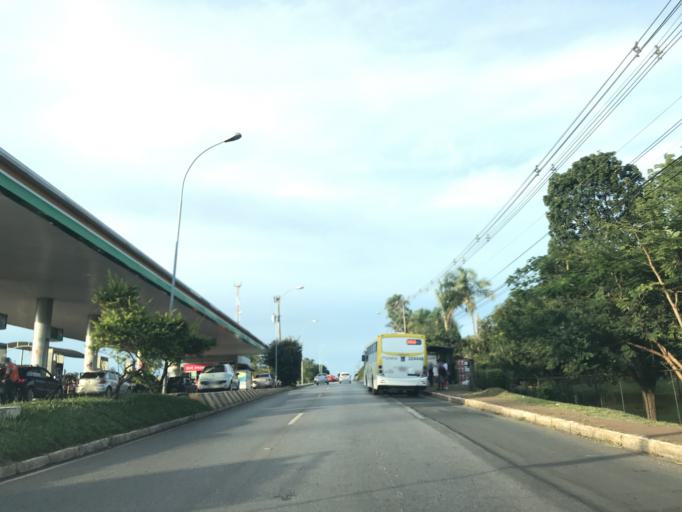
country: BR
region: Federal District
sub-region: Brasilia
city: Brasilia
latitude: -15.8319
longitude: -47.8133
